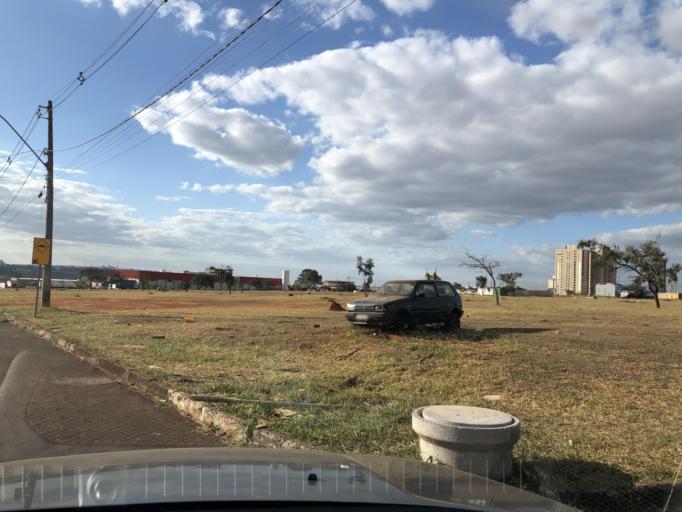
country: BR
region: Federal District
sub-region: Brasilia
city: Brasilia
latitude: -15.8751
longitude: -48.0911
